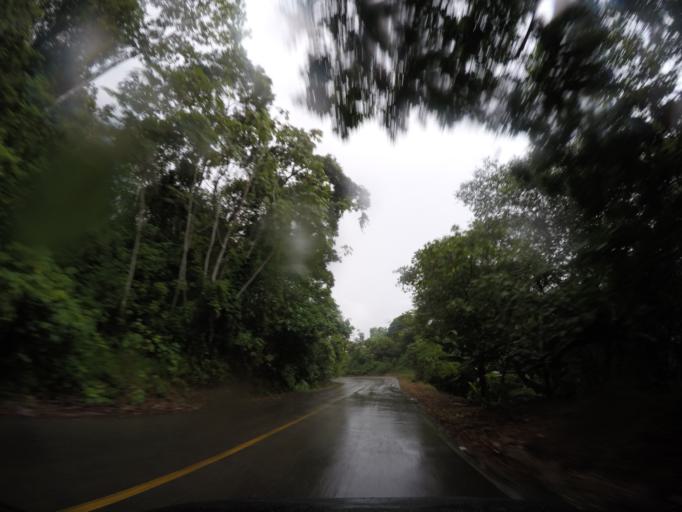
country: MX
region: Oaxaca
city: San Gabriel Mixtepec
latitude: 16.0812
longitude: -97.0797
